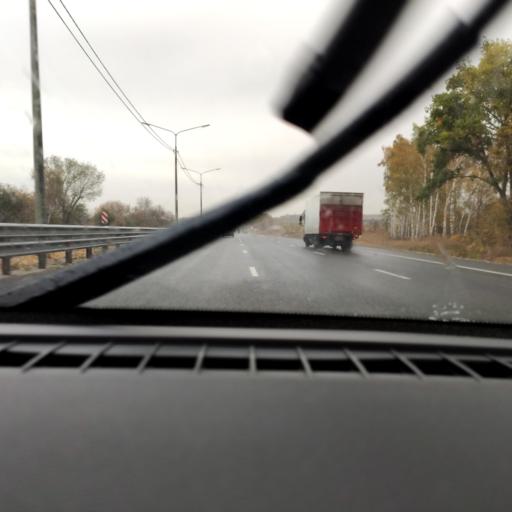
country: RU
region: Voronezj
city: Podgornoye
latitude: 51.8211
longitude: 39.2097
